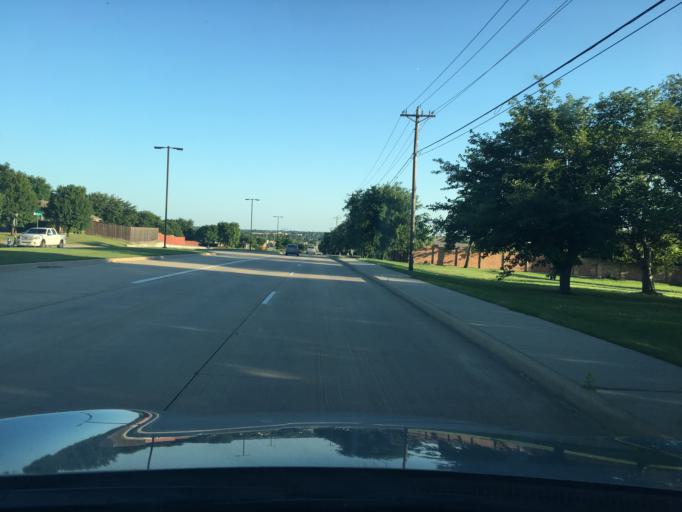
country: US
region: Texas
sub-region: Collin County
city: McKinney
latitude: 33.2254
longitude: -96.6791
